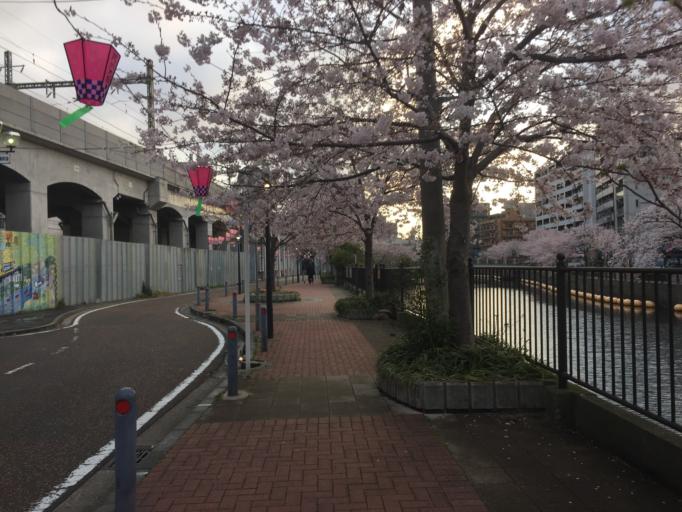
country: JP
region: Kanagawa
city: Yokohama
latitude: 35.4402
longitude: 139.6242
